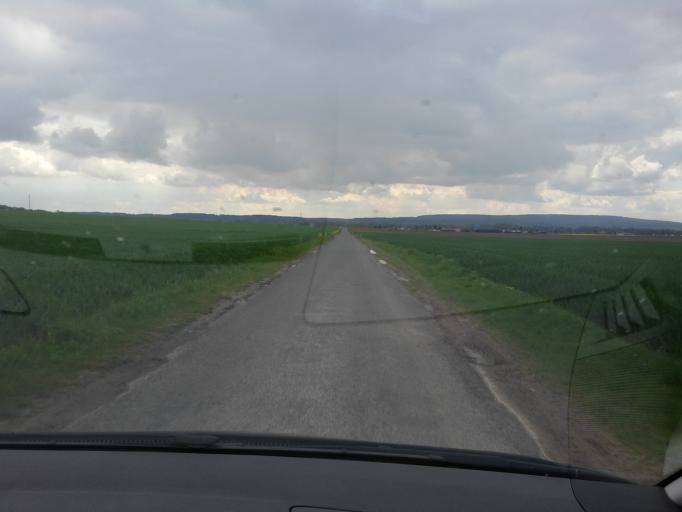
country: FR
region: Picardie
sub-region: Departement de l'Oise
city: Chevrieres
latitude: 49.3643
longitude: 2.6841
